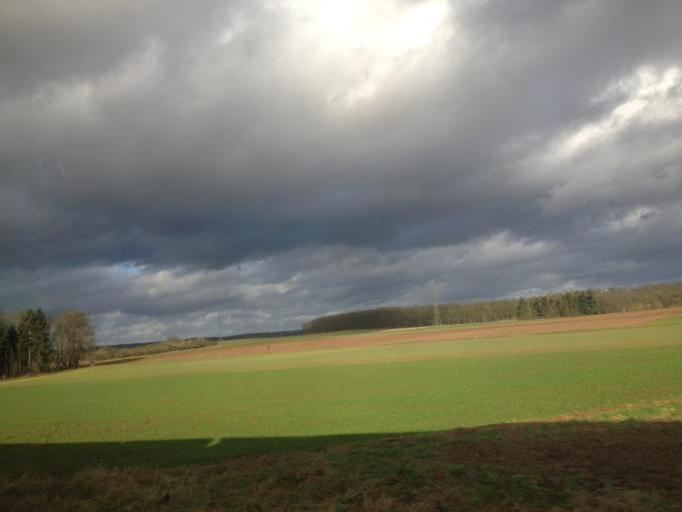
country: DE
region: Hesse
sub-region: Regierungsbezirk Giessen
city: Lich
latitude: 50.5067
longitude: 8.8450
